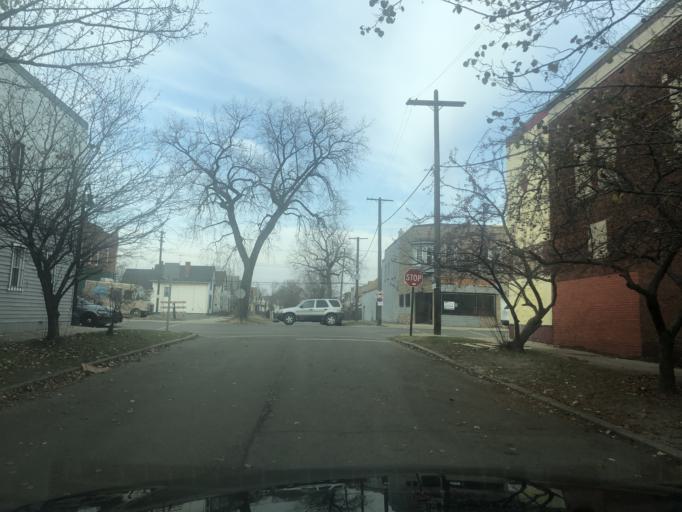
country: US
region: Michigan
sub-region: Wayne County
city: River Rouge
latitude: 42.3179
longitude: -83.1004
